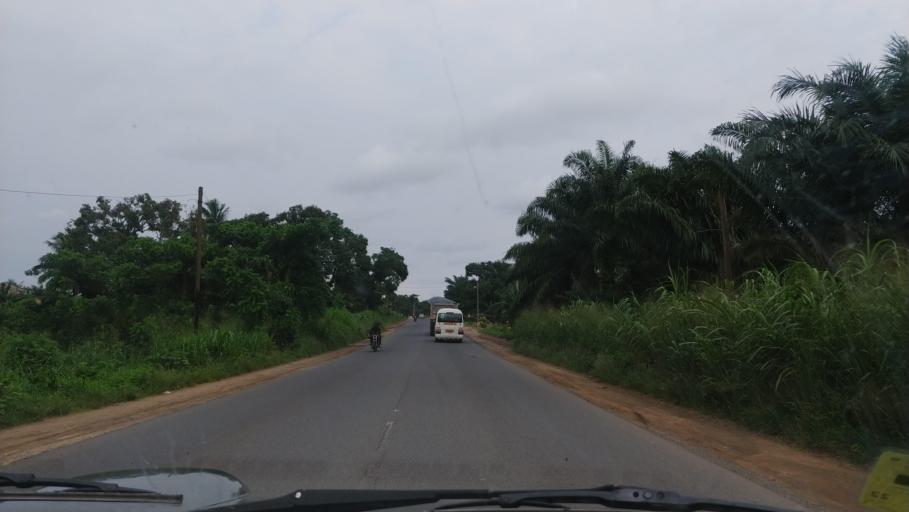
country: CM
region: Littoral
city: Dibombari
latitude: 4.1548
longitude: 9.5872
